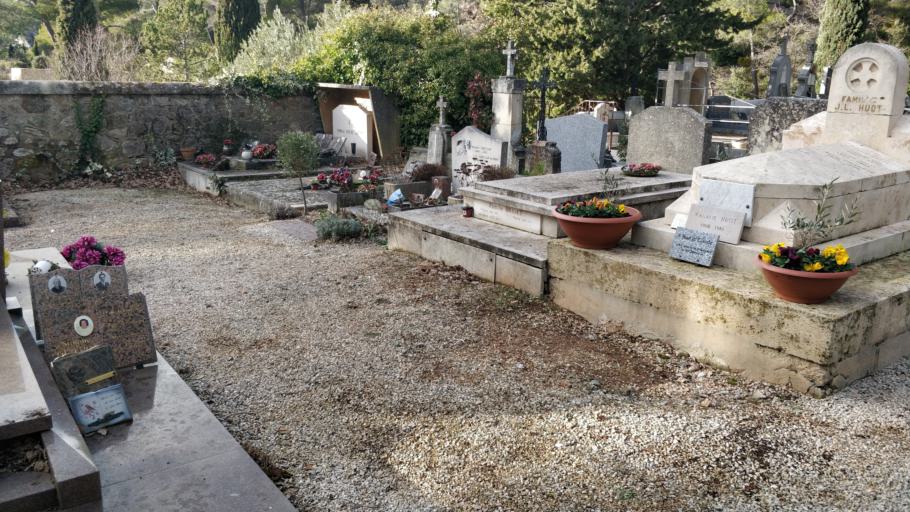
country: FR
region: Provence-Alpes-Cote d'Azur
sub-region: Departement des Bouches-du-Rhone
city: Le Tholonet
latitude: 43.5240
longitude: 5.5146
